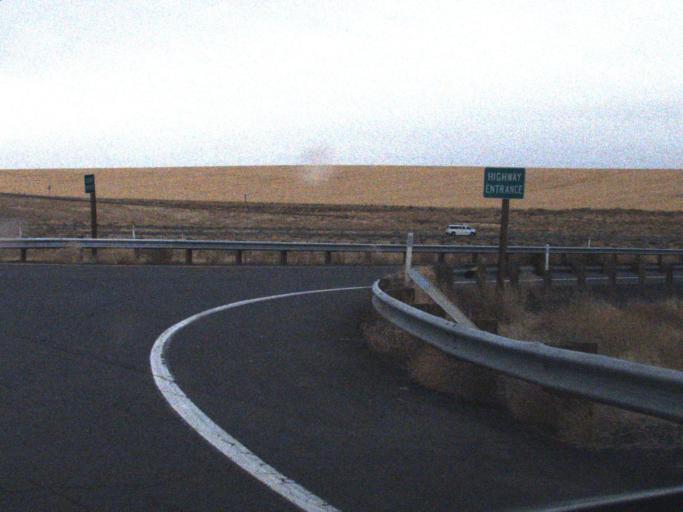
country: US
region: Washington
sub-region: Franklin County
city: Connell
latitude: 46.7914
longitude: -118.7528
